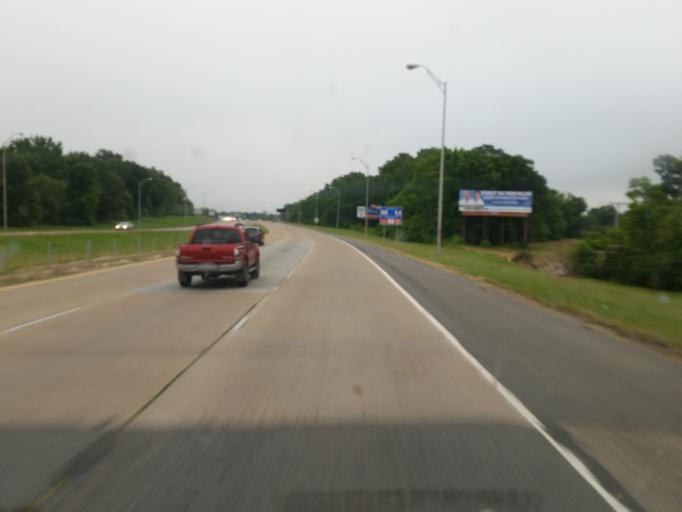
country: US
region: Louisiana
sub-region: Caddo Parish
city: Shreveport
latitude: 32.4637
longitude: -93.8205
